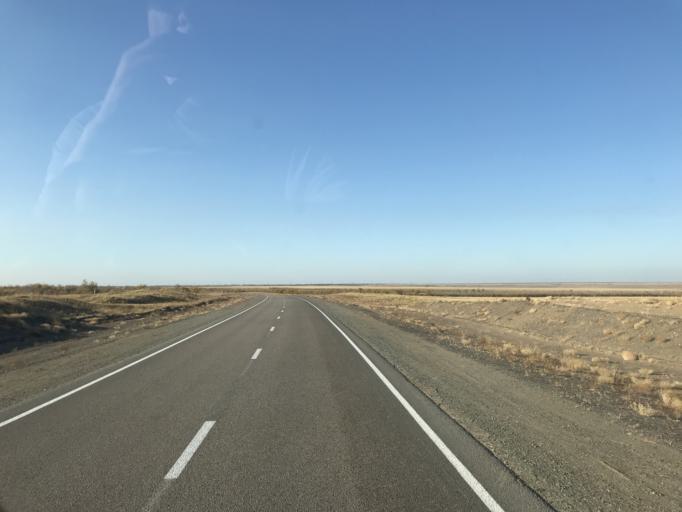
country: KZ
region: Pavlodar
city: Koktobe
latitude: 51.8567
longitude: 77.4506
